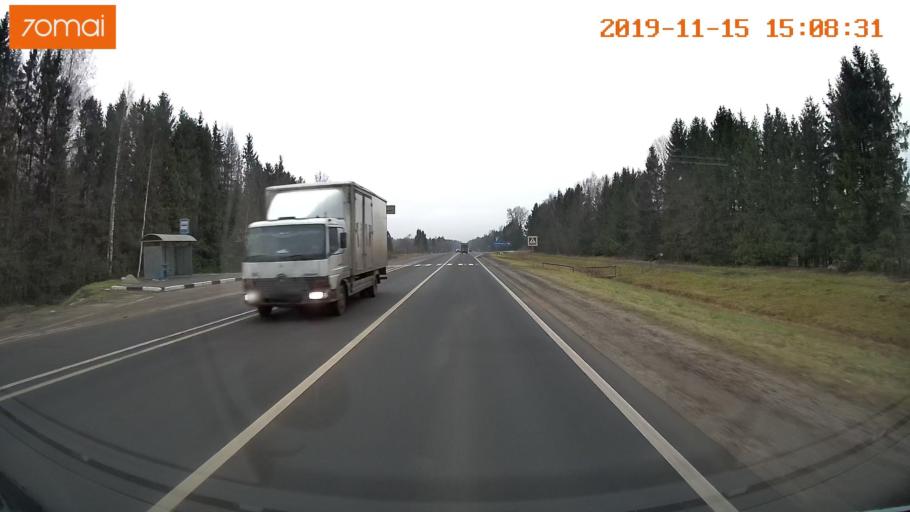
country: RU
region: Jaroslavl
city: Prechistoye
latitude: 58.3697
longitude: 40.2757
